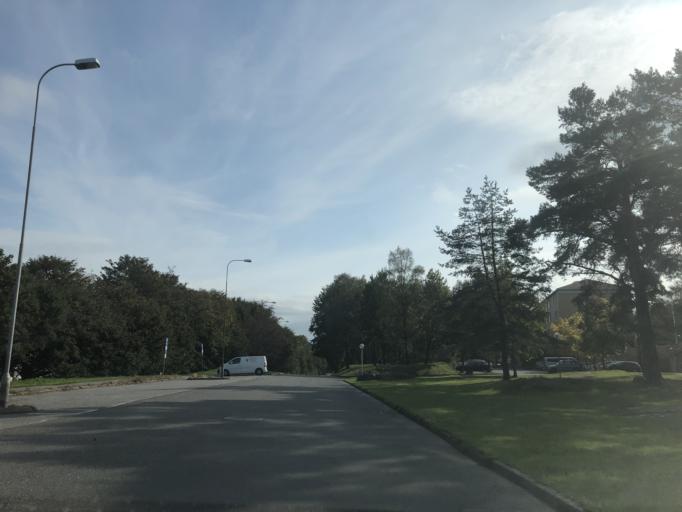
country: SE
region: Vaestra Goetaland
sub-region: Goteborg
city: Majorna
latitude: 57.6557
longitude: 11.8978
